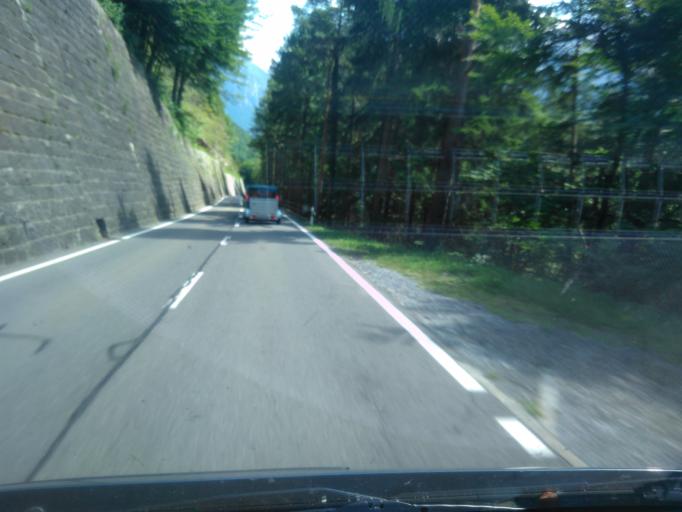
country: CH
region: Bern
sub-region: Interlaken-Oberhasli District
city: Meiringen
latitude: 46.7446
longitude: 8.1566
